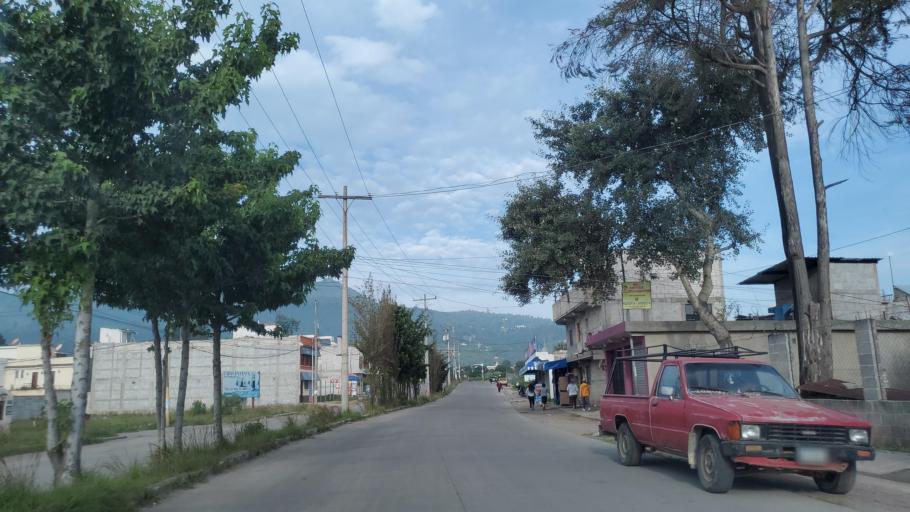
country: GT
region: Quetzaltenango
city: Quetzaltenango
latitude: 14.8323
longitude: -91.5398
